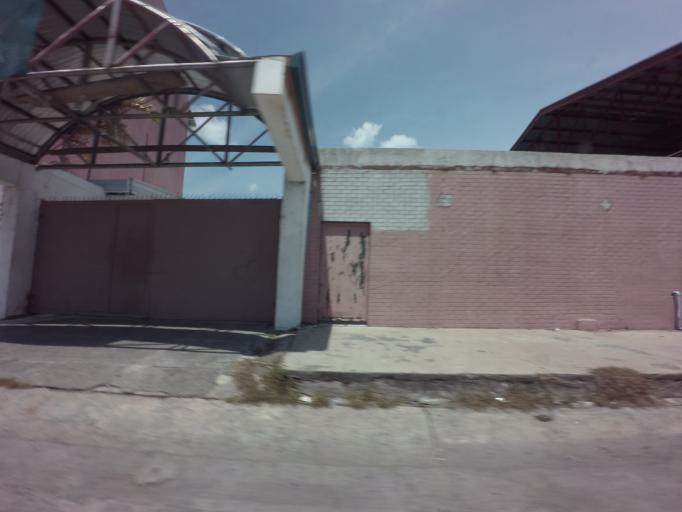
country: PH
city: Sambayanihan People's Village
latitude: 14.4254
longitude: 121.0127
